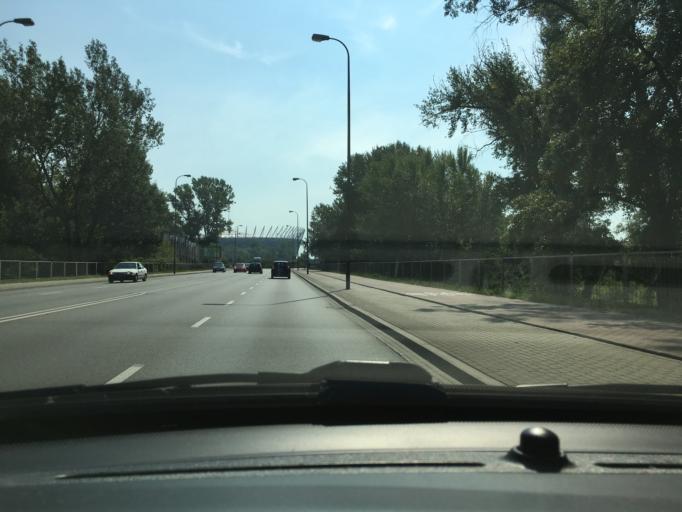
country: PL
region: Masovian Voivodeship
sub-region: Warszawa
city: Praga Polnoc
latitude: 52.2458
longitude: 21.0330
